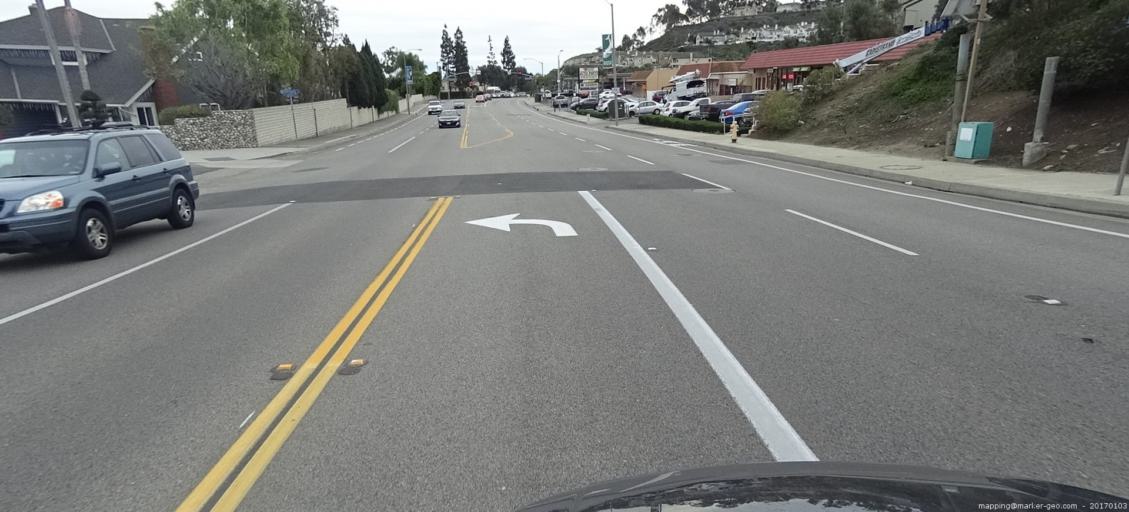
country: US
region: California
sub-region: Orange County
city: Dana Point
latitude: 33.4773
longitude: -117.6855
